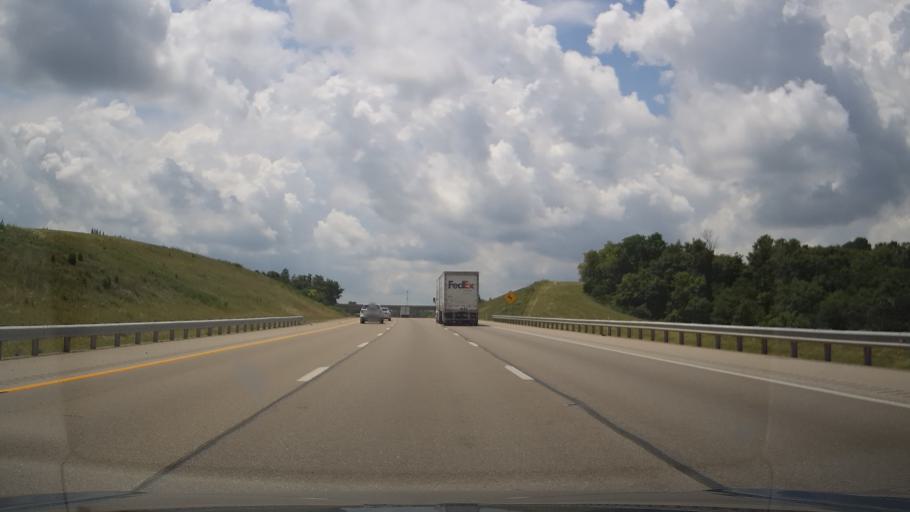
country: US
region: Kentucky
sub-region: Grant County
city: Williamstown
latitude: 38.5797
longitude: -84.5906
